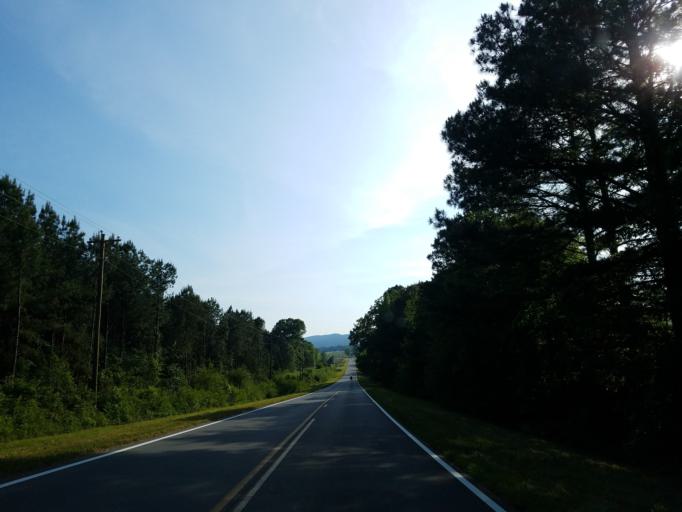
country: US
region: Georgia
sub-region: Chattooga County
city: Trion
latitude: 34.5213
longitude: -85.2204
